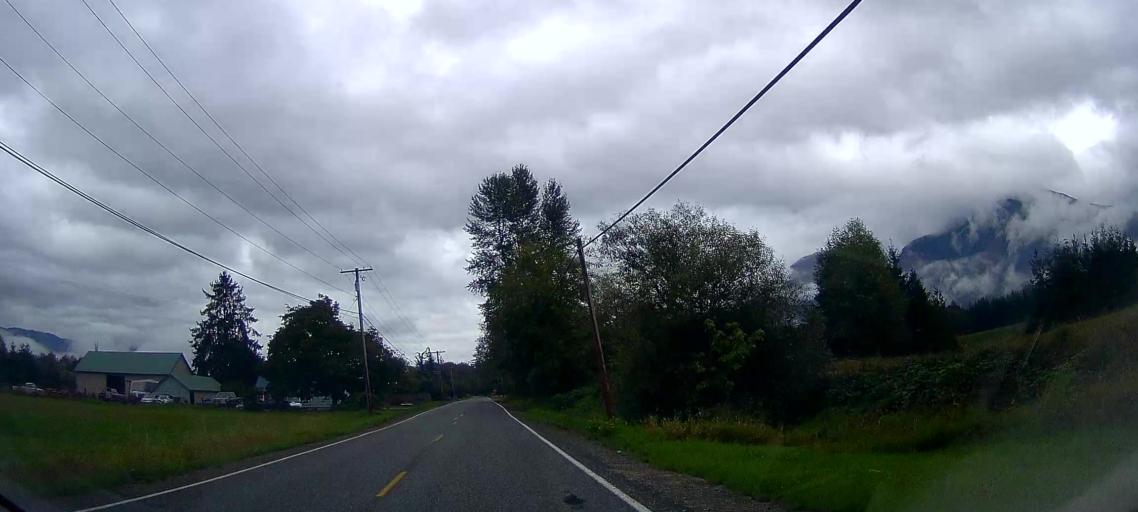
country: US
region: Washington
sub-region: Skagit County
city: Sedro-Woolley
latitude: 48.5270
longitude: -122.0340
